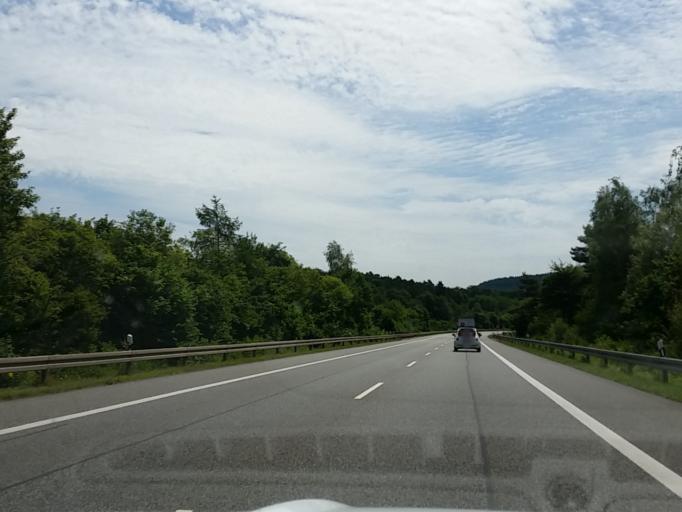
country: DE
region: Saarland
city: Losheim
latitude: 49.5081
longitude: 6.7879
